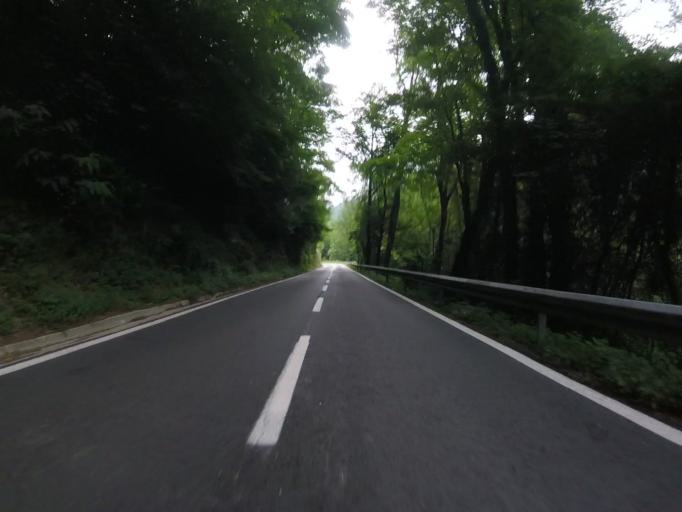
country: ES
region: Navarre
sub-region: Provincia de Navarra
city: Zubieta
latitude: 43.1262
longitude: -1.7460
